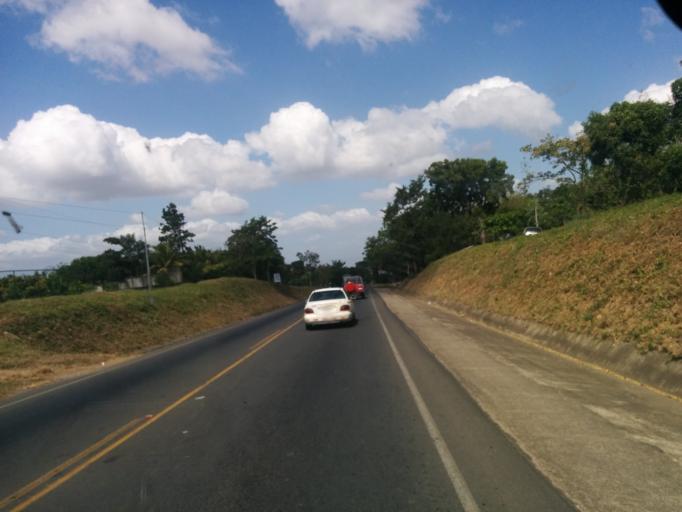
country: NI
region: Masaya
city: Masaya
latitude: 11.9486
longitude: -86.0917
